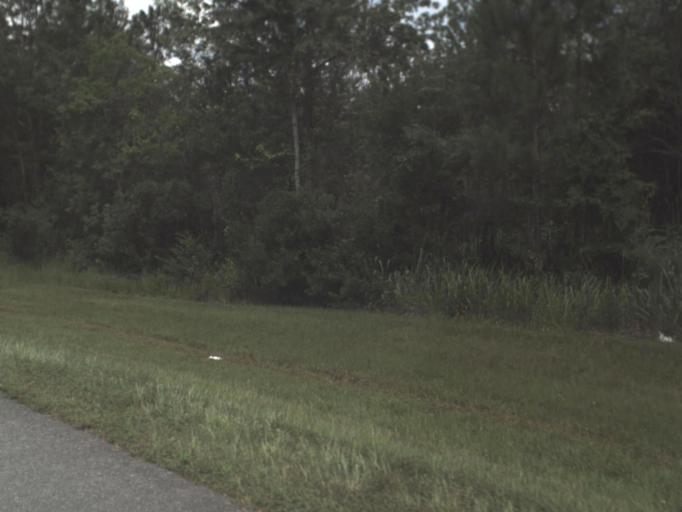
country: US
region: Florida
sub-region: Union County
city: Lake Butler
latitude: 30.0491
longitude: -82.2669
